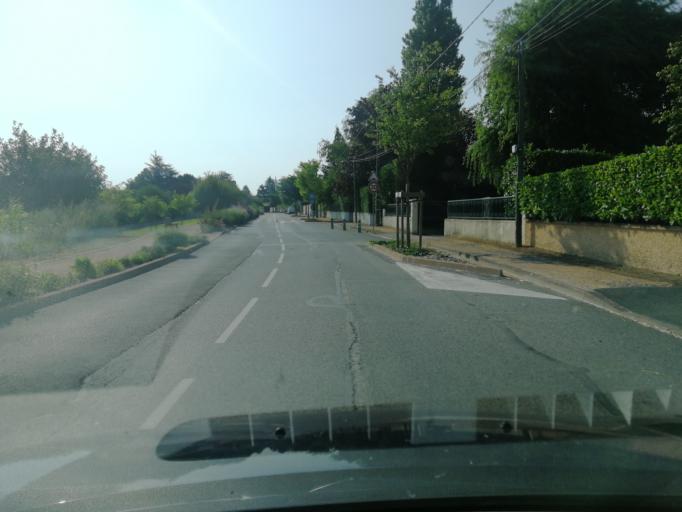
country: FR
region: Rhone-Alpes
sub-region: Departement du Rhone
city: Sathonay-Village
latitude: 45.8365
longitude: 4.8733
